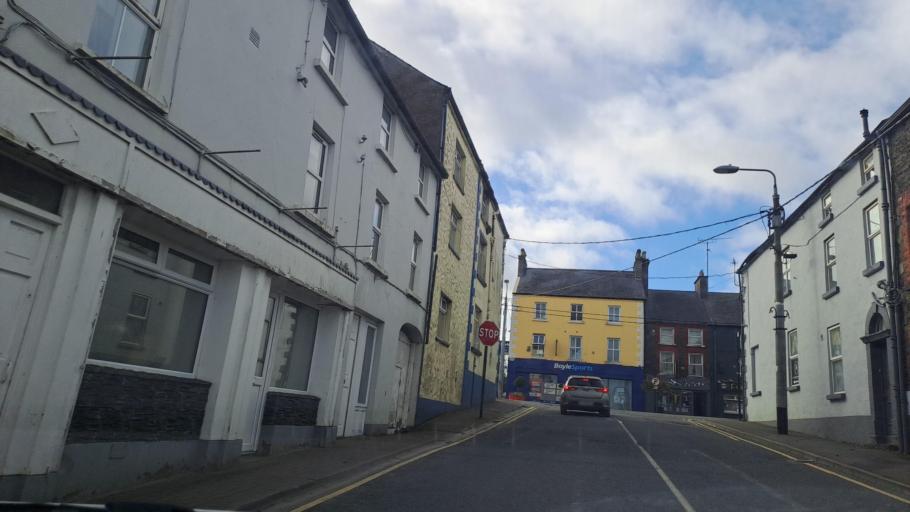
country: IE
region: Ulster
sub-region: An Cabhan
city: Bailieborough
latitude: 53.9163
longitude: -6.9686
